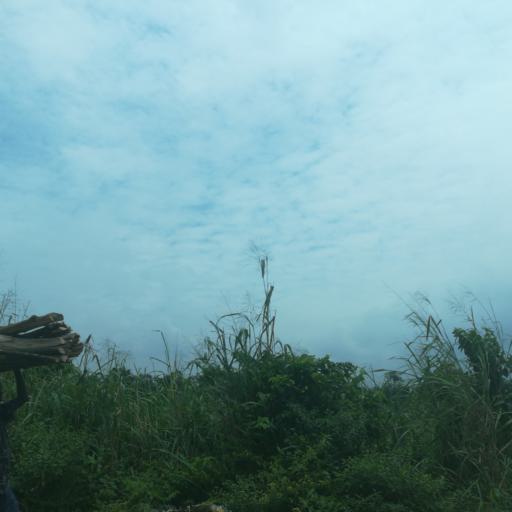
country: NG
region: Lagos
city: Ejirin
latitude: 6.6623
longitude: 3.7937
